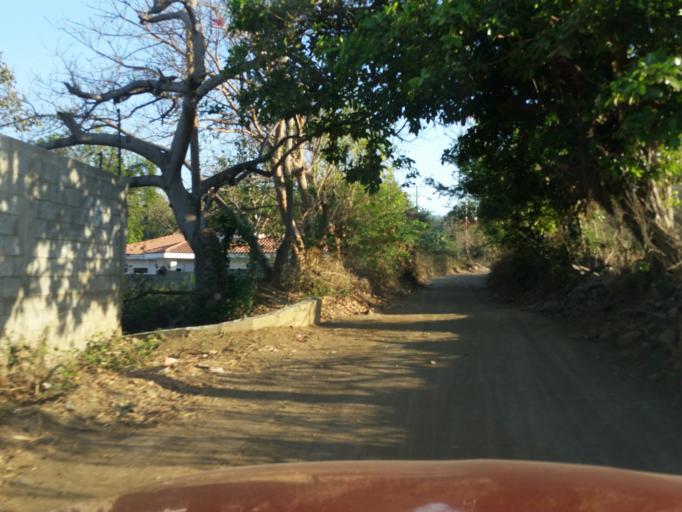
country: NI
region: Managua
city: Managua
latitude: 12.0748
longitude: -86.2540
